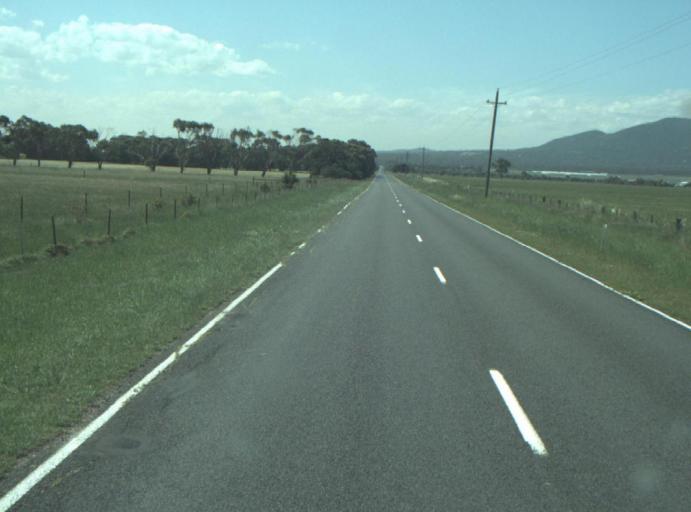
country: AU
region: Victoria
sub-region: Greater Geelong
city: Lara
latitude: -37.9926
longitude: 144.4018
